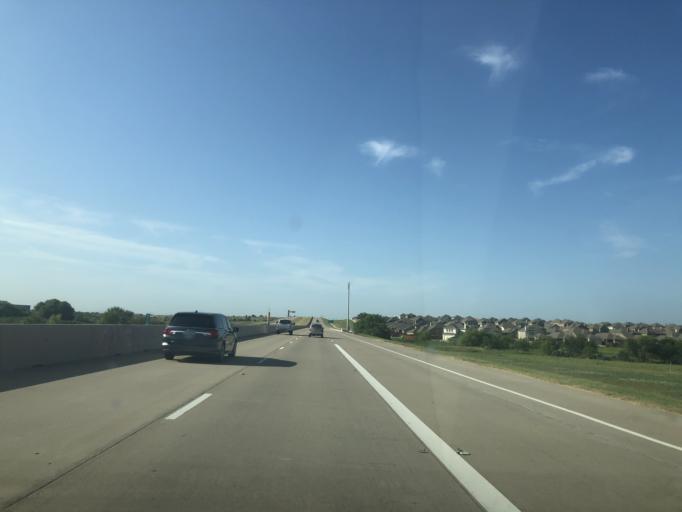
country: US
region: Texas
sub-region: Tarrant County
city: Crowley
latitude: 32.6243
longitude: -97.4127
